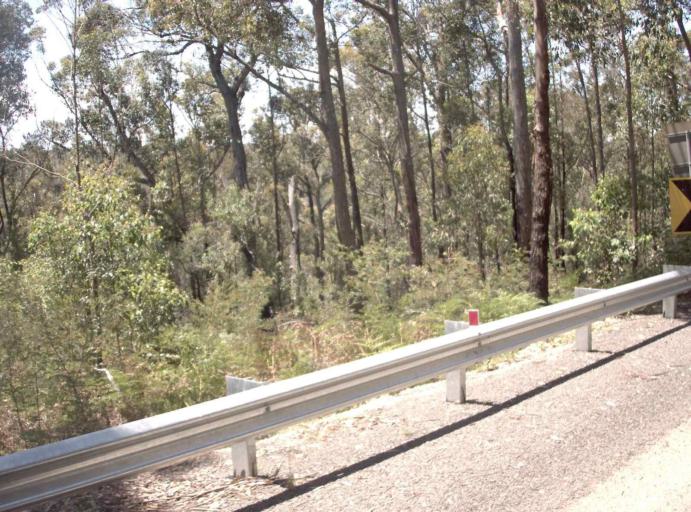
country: AU
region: Victoria
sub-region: East Gippsland
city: Lakes Entrance
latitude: -37.6957
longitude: 148.7345
